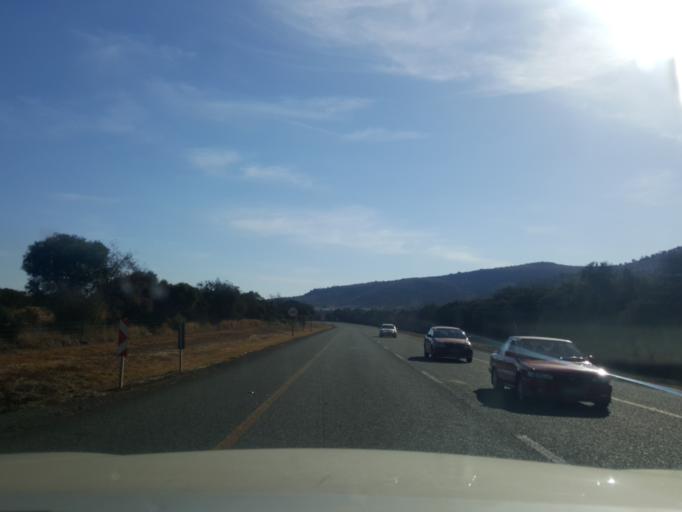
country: ZA
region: North-West
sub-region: Ngaka Modiri Molema District Municipality
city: Zeerust
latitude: -25.5421
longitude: 26.1140
